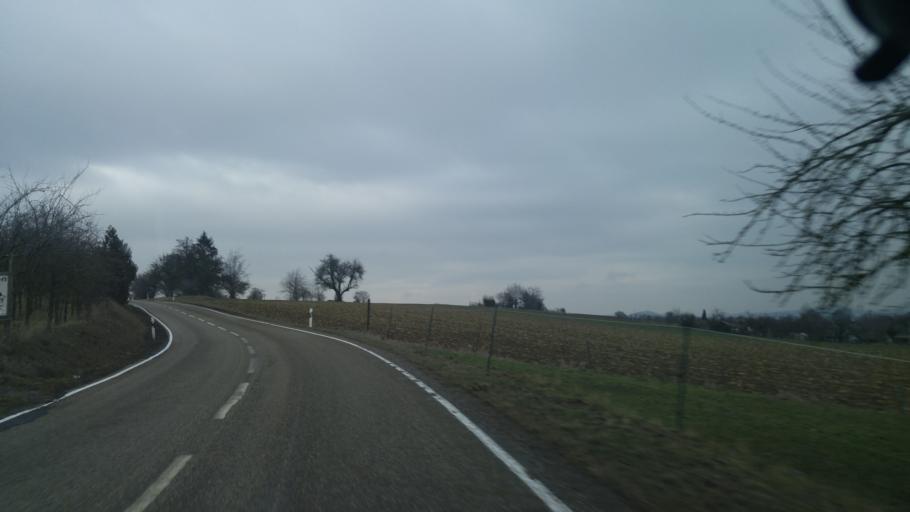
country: DE
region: Baden-Wuerttemberg
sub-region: Regierungsbezirk Stuttgart
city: Leonberg
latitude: 48.8235
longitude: 9.0189
